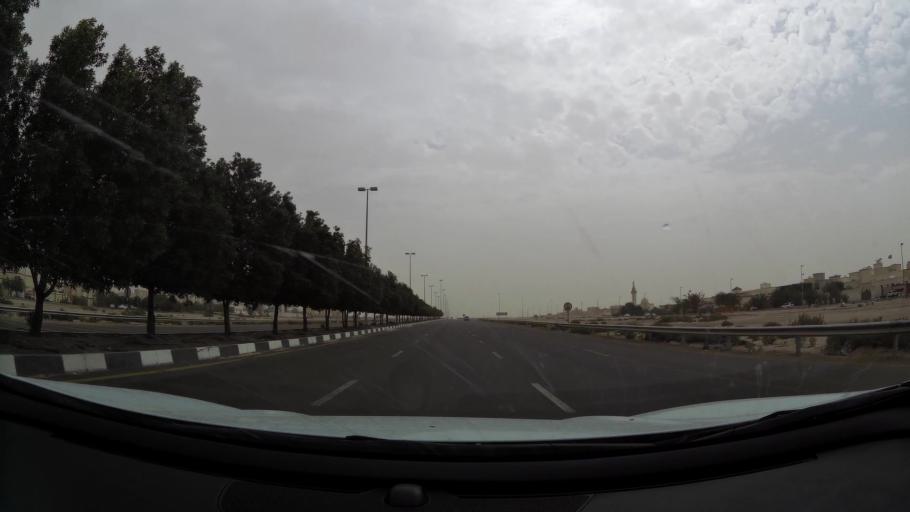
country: AE
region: Abu Dhabi
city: Abu Dhabi
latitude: 24.3831
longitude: 54.7240
